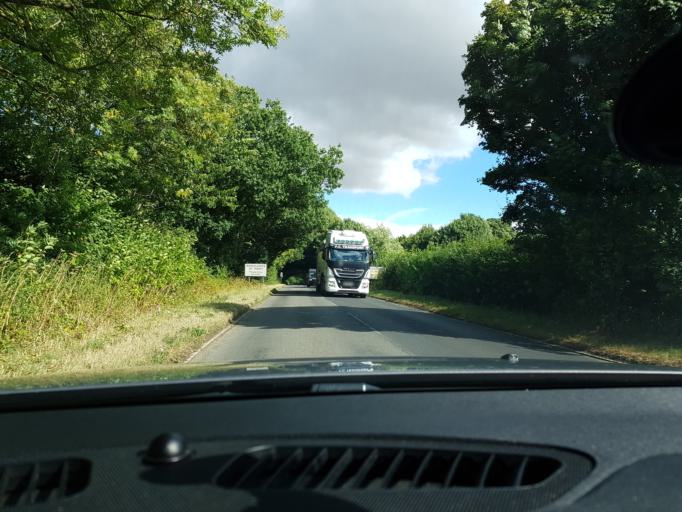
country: GB
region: England
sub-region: West Berkshire
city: Lambourn
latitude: 51.4745
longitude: -1.5238
